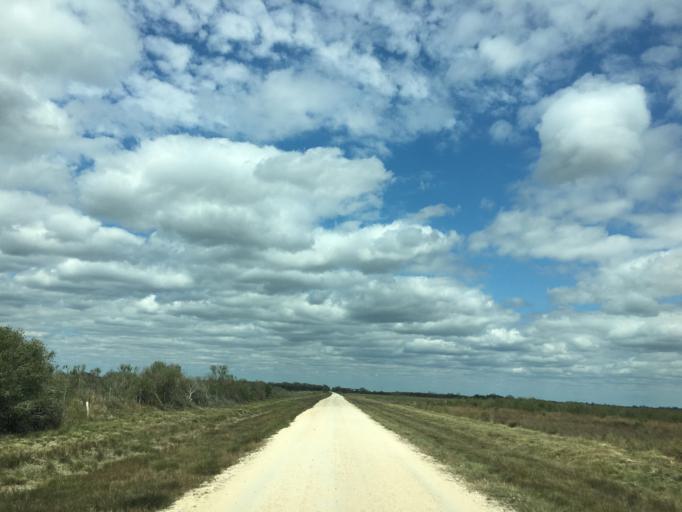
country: US
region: Texas
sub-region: Brazoria County
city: Oyster Creek
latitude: 29.0477
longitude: -95.2683
